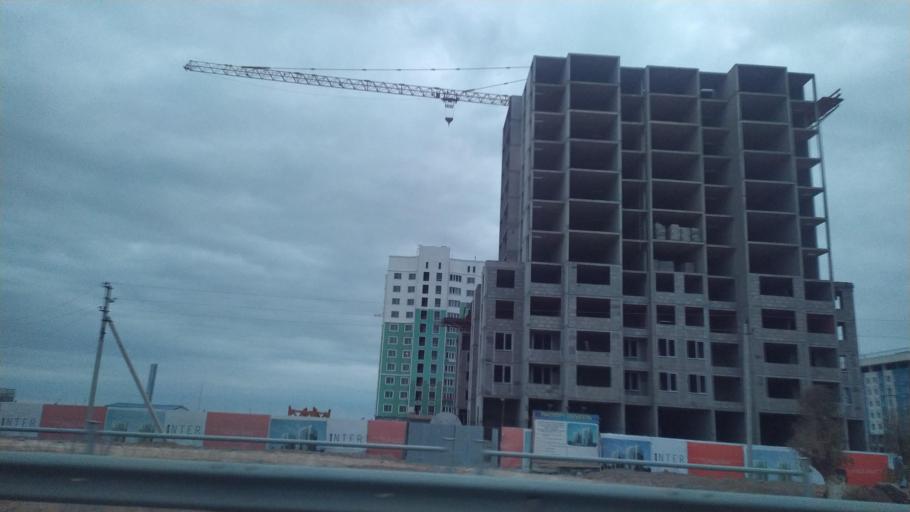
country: KZ
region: Ongtustik Qazaqstan
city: Turkestan
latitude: 43.2703
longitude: 68.3496
